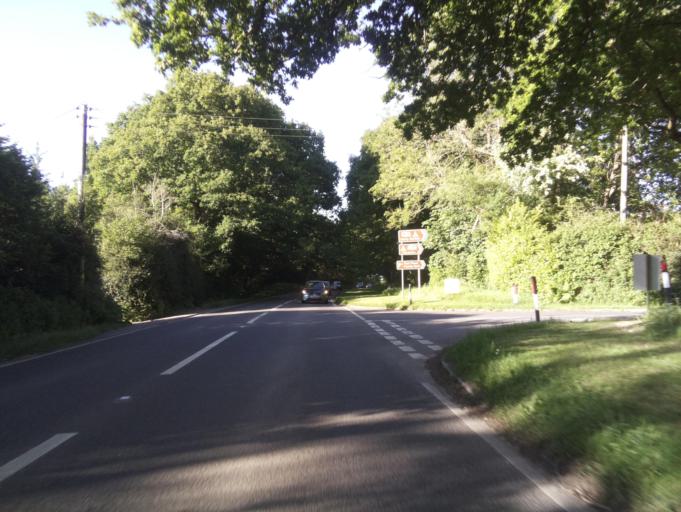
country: GB
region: England
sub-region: Devon
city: Sidmouth
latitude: 50.7062
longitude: -3.1811
